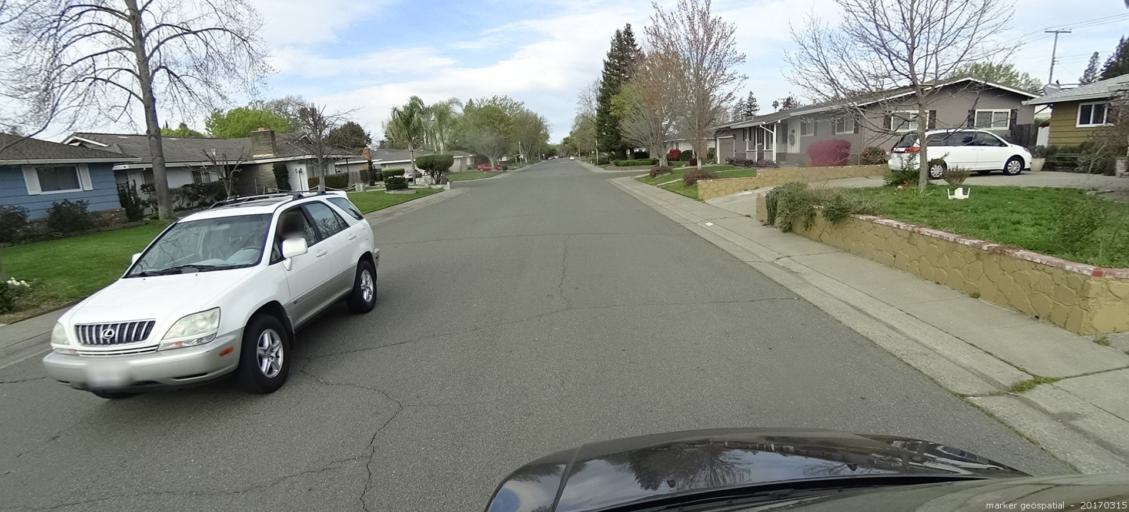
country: US
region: California
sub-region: Sacramento County
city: Parkway
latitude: 38.5104
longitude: -121.5076
